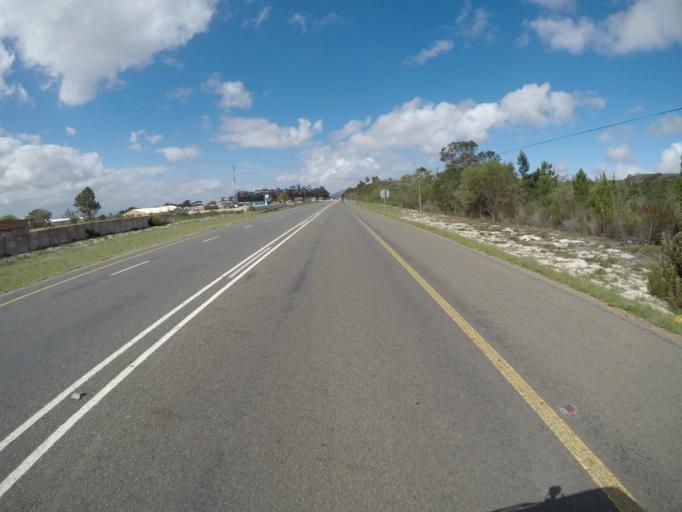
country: ZA
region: Western Cape
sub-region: Eden District Municipality
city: Riversdale
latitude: -34.2127
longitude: 21.5820
